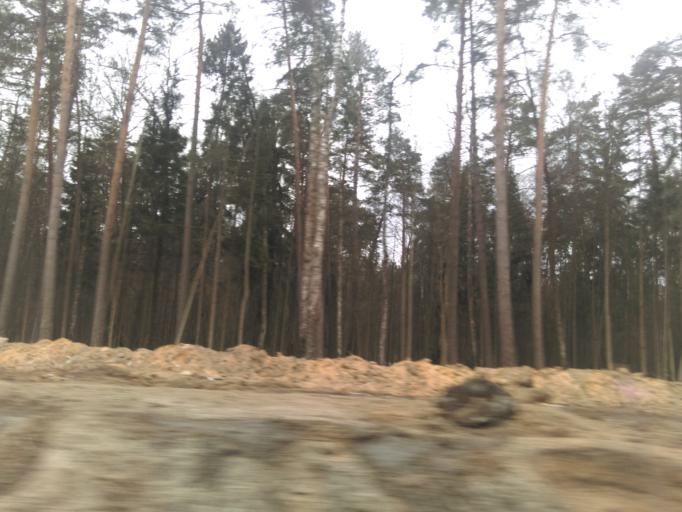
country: RU
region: Moskovskaya
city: Gorki Vtoryye
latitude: 55.7241
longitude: 37.1860
